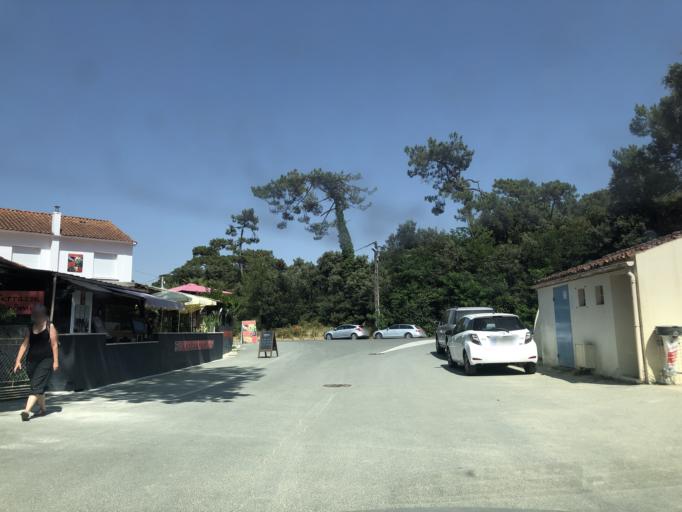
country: FR
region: Poitou-Charentes
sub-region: Departement de la Charente-Maritime
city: Meschers-sur-Gironde
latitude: 45.5682
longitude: -0.9718
